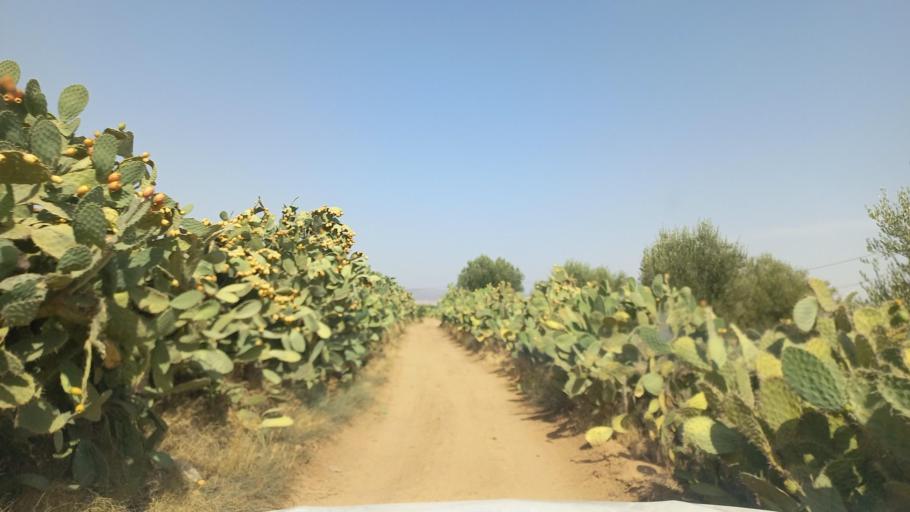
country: TN
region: Al Qasrayn
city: Kasserine
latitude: 35.2379
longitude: 9.0529
